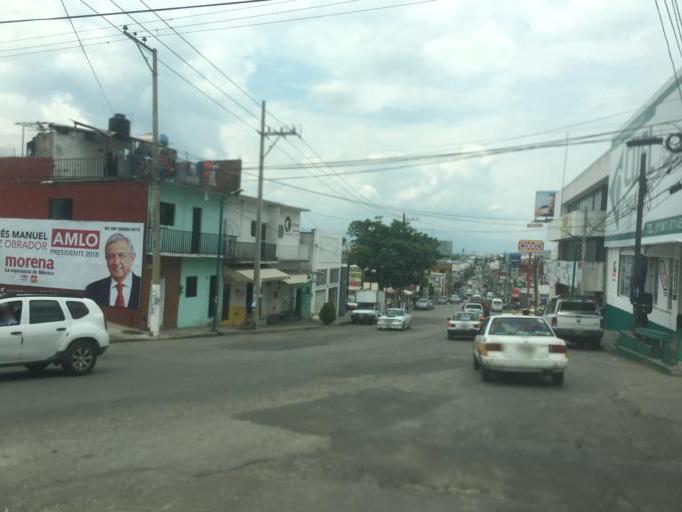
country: MX
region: Chiapas
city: Tuxtla Gutierrez
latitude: 16.7474
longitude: -93.1254
